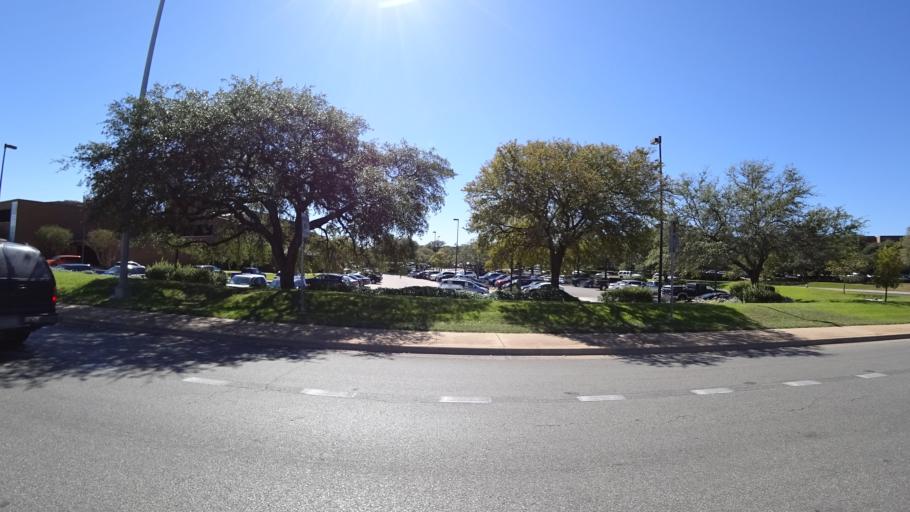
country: US
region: Texas
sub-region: Travis County
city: West Lake Hills
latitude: 30.3522
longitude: -97.7506
